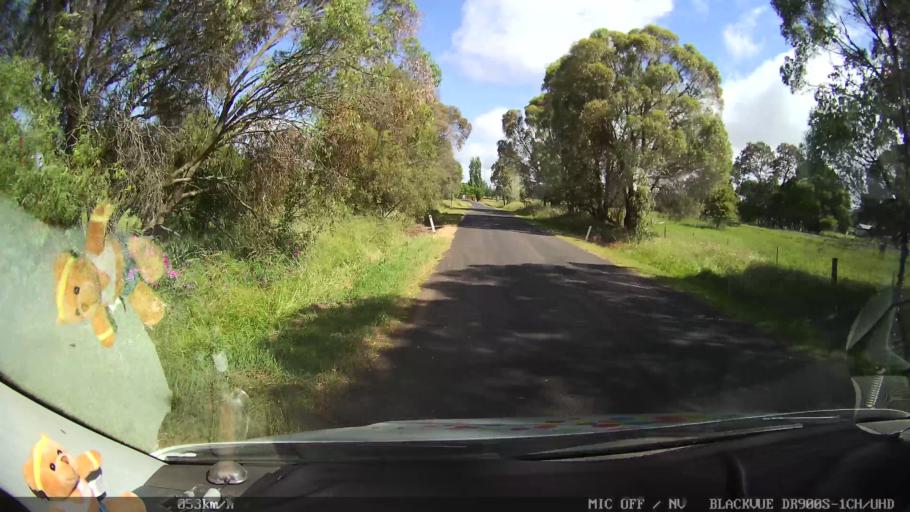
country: AU
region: New South Wales
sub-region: Guyra
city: Guyra
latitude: -30.0259
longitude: 151.6613
